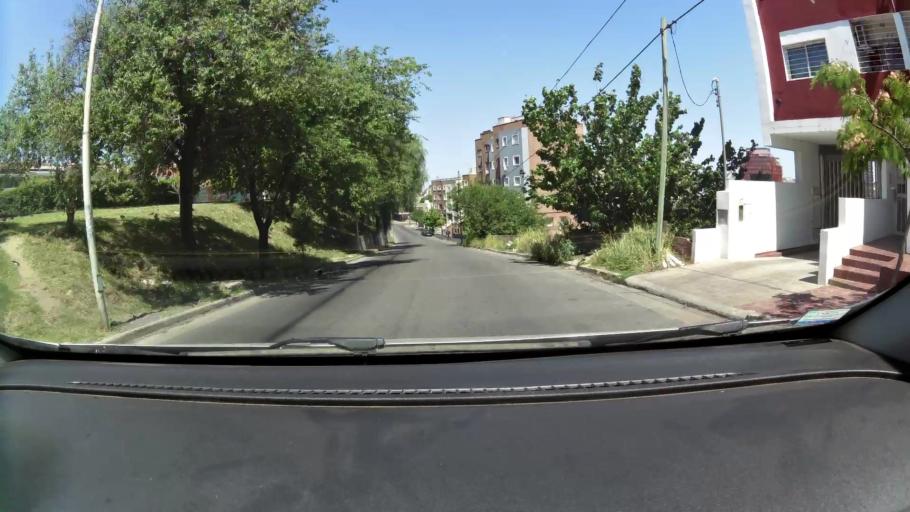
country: AR
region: Cordoba
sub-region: Departamento de Capital
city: Cordoba
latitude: -31.4034
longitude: -64.1891
